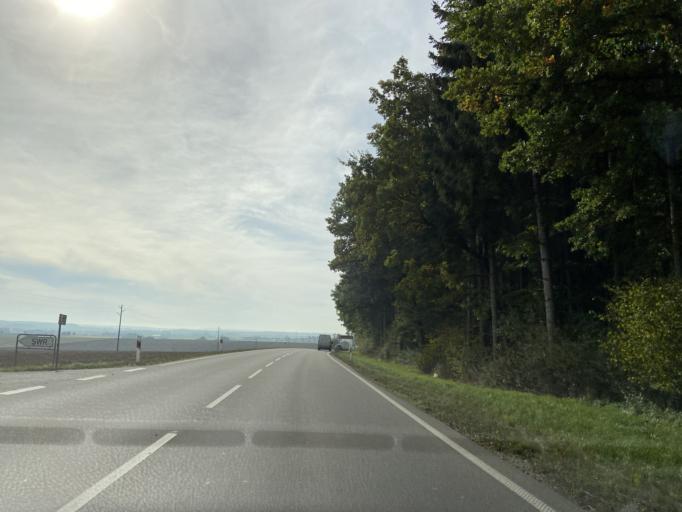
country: DE
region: Baden-Wuerttemberg
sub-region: Tuebingen Region
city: Messkirch
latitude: 48.0337
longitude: 9.1151
